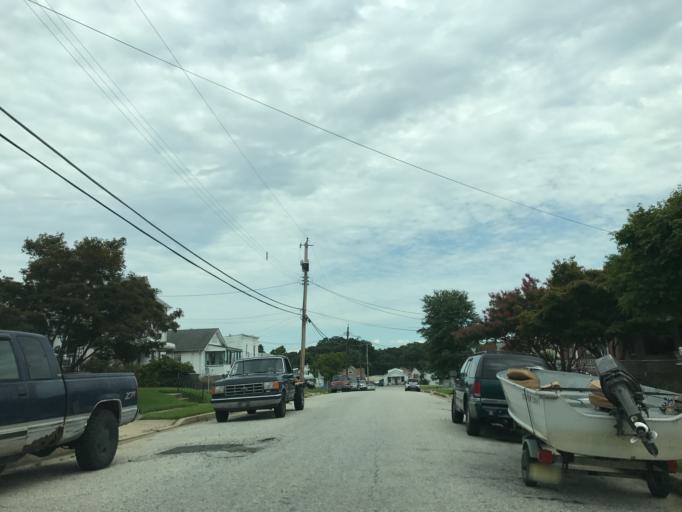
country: US
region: Maryland
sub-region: Baltimore County
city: Essex
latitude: 39.3151
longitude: -76.4779
